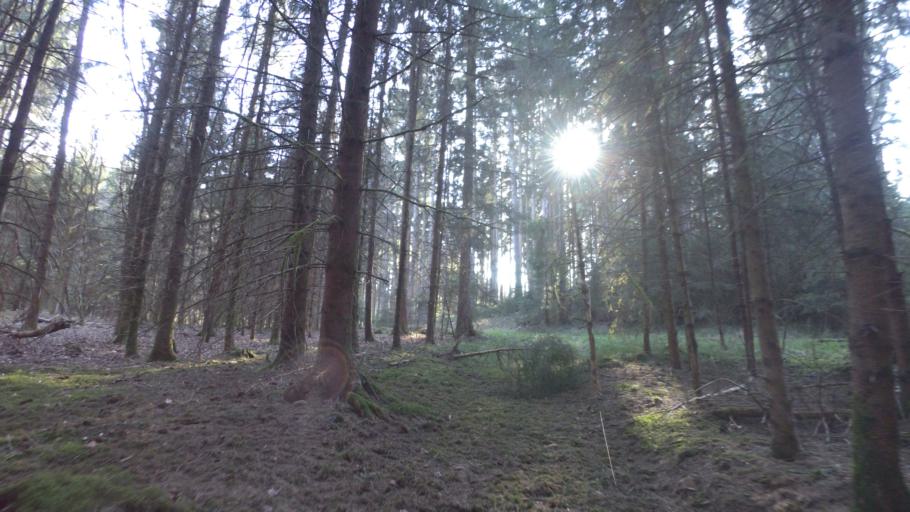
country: DE
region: Bavaria
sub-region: Upper Bavaria
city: Nussdorf
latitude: 47.9289
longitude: 12.5809
